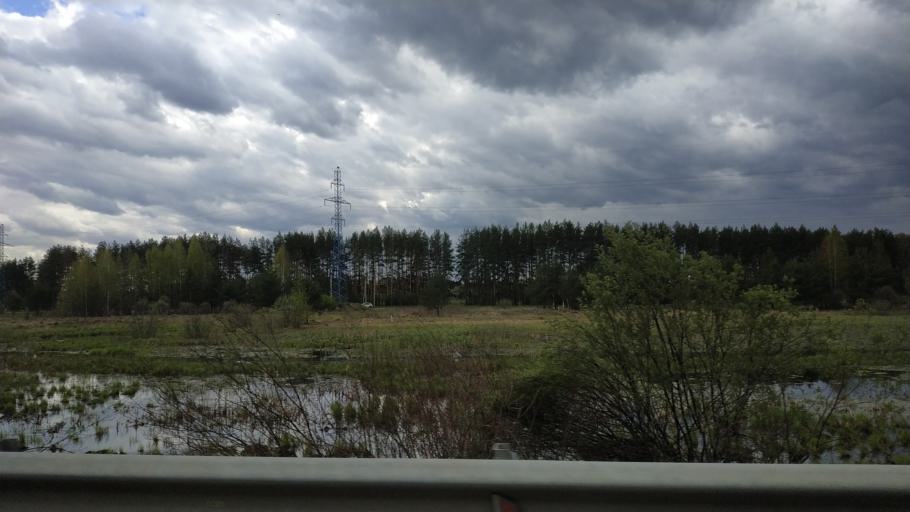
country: RU
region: Moskovskaya
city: Pavlovskiy Posad
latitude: 55.8019
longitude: 38.6782
